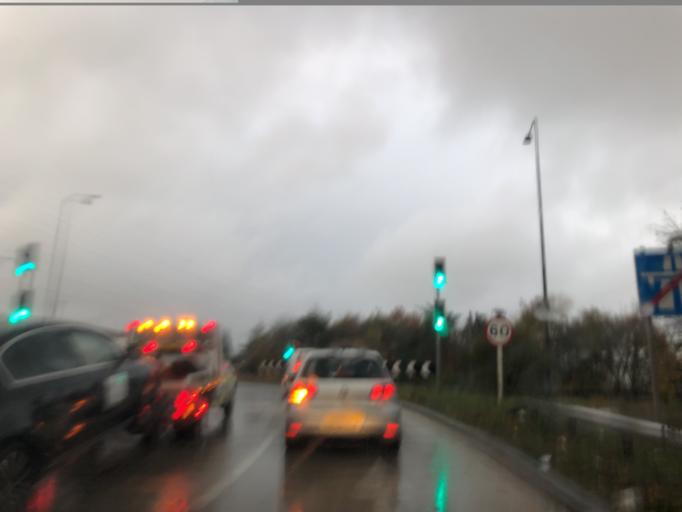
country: GB
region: England
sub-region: Solihull
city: Bickenhill
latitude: 52.4439
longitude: -1.7111
